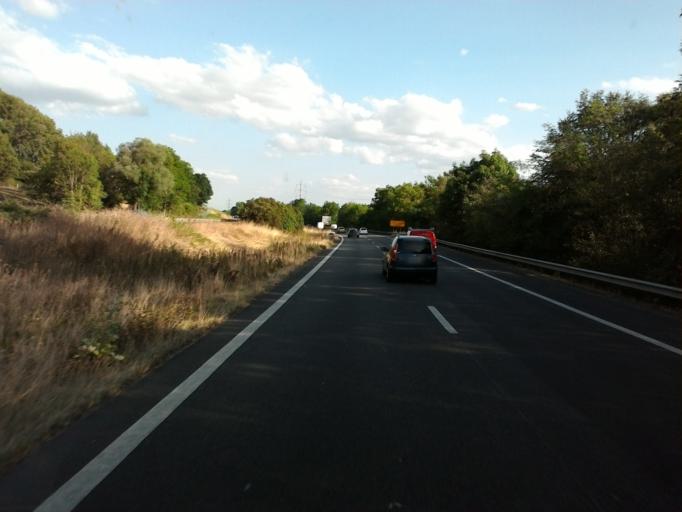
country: FR
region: Lorraine
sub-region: Departement de Meurthe-et-Moselle
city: Frouard
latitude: 48.7664
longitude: 6.1441
